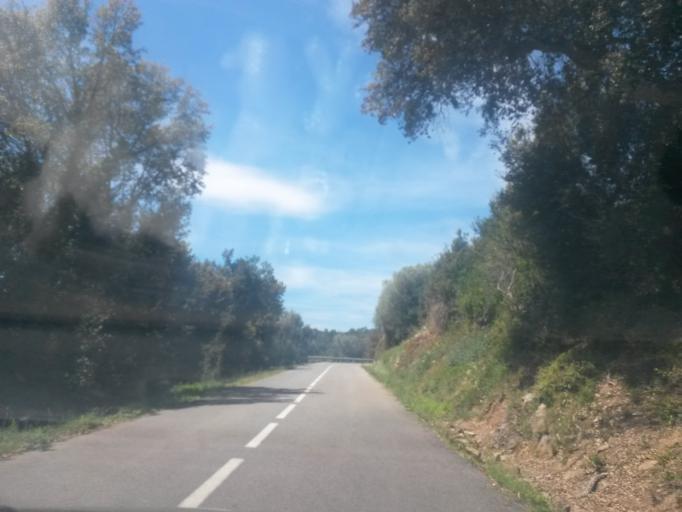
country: ES
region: Catalonia
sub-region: Provincia de Girona
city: Madremanya
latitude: 41.9391
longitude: 2.9370
